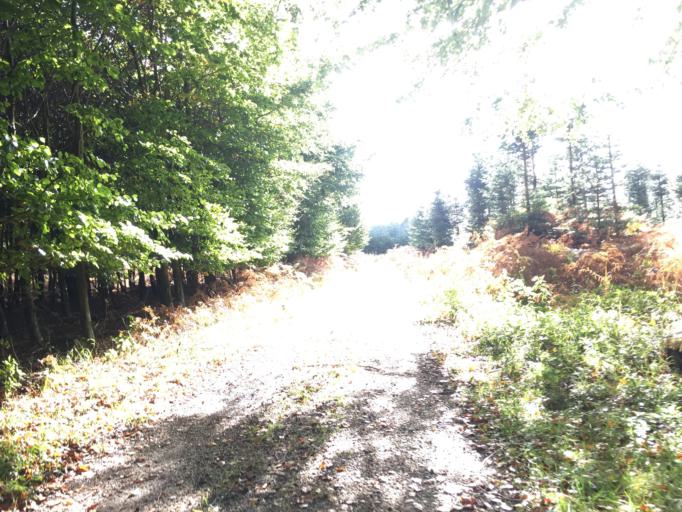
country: DK
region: Zealand
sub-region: Koge Kommune
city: Borup
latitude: 55.4660
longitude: 11.8981
